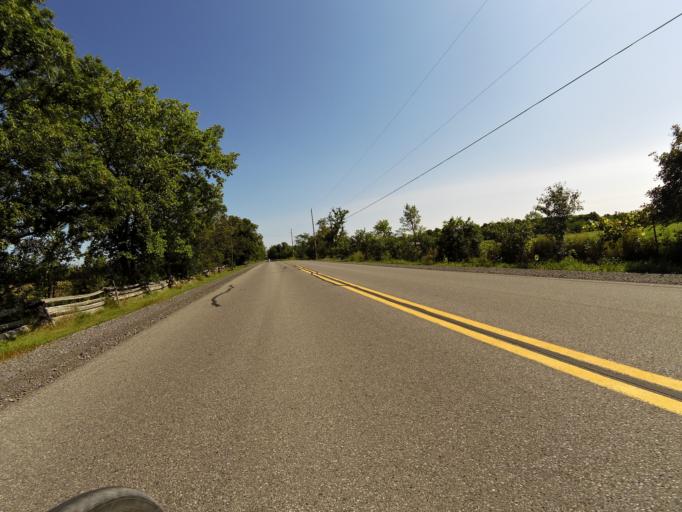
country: CA
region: Ontario
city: Bells Corners
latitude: 45.4224
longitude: -75.9491
